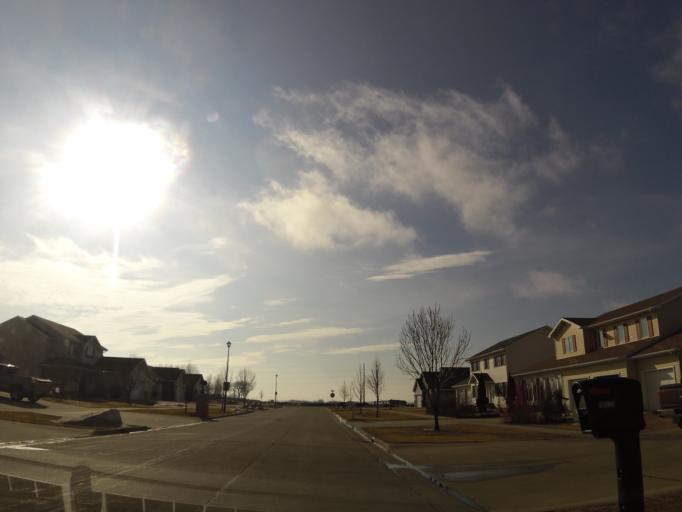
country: US
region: North Dakota
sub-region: Grand Forks County
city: Grand Forks
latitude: 47.8778
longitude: -97.0626
